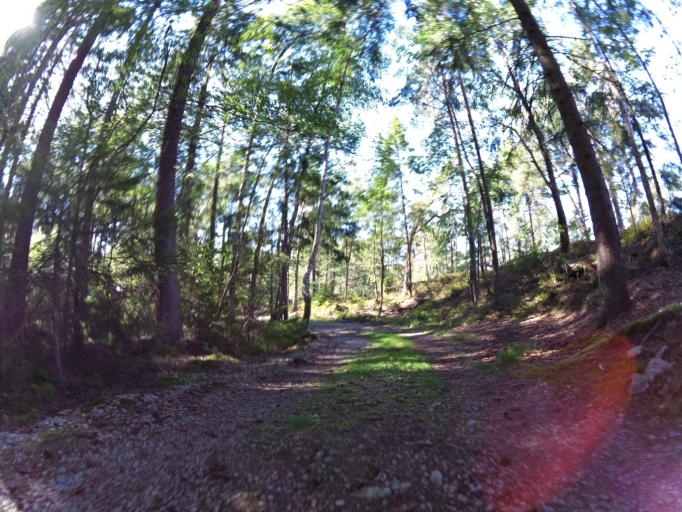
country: NO
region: Ostfold
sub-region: Fredrikstad
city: Fredrikstad
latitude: 59.1692
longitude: 10.8455
